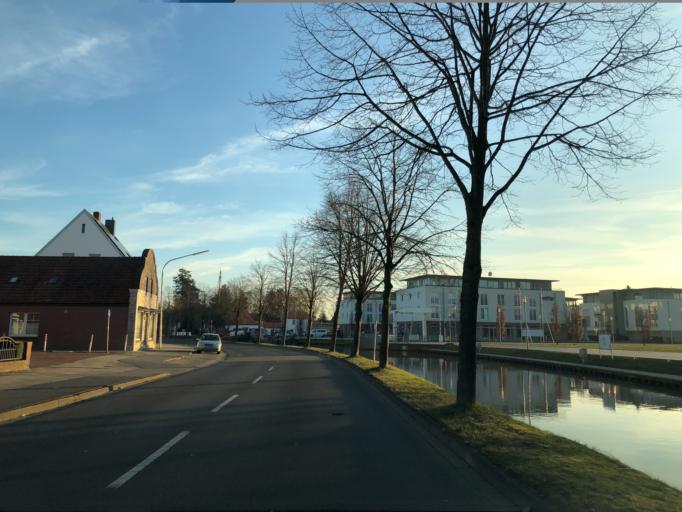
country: DE
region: Lower Saxony
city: Papenburg
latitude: 53.0874
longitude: 7.3885
